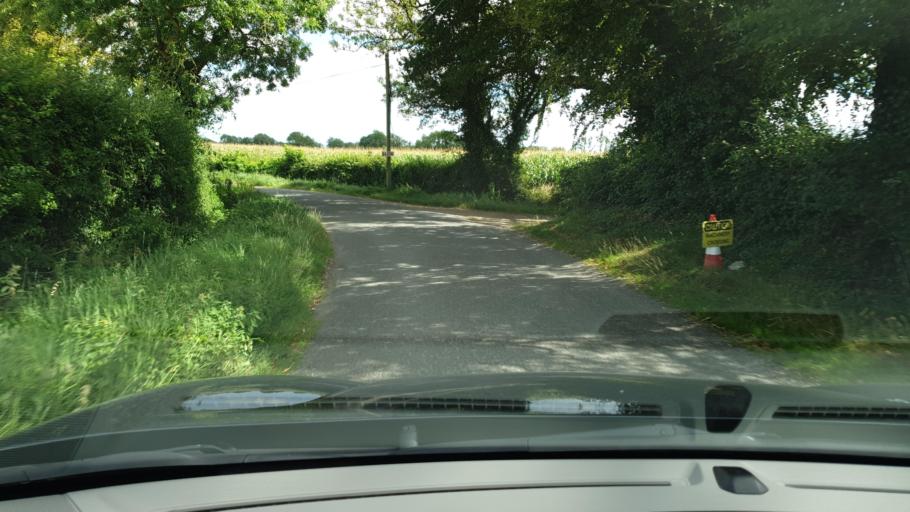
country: IE
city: Confey
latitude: 53.3904
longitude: -6.4809
